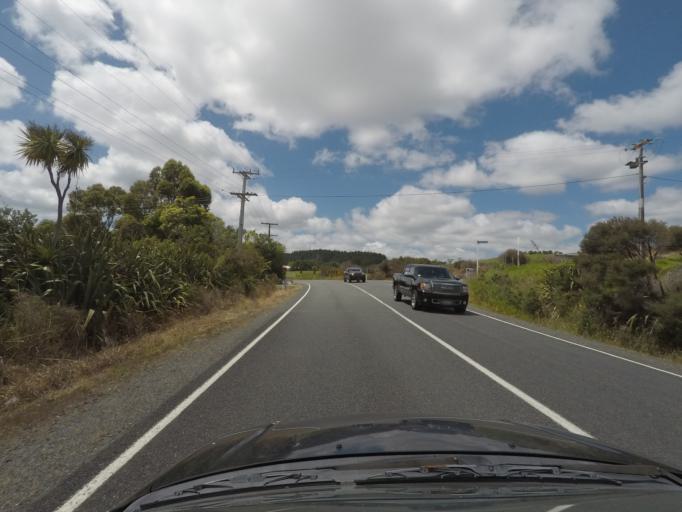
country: NZ
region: Northland
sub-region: Whangarei
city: Ruakaka
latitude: -36.0136
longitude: 174.4835
